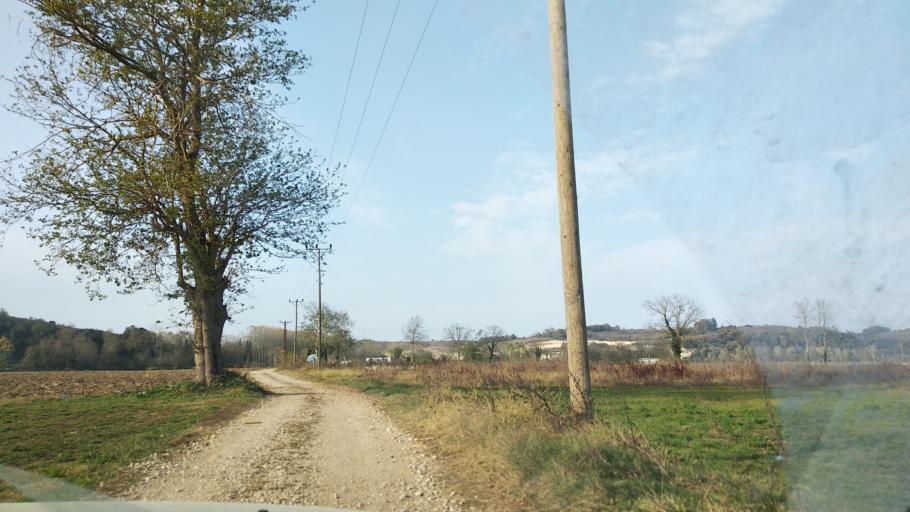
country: TR
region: Sakarya
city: Karasu
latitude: 41.0896
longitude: 30.5963
